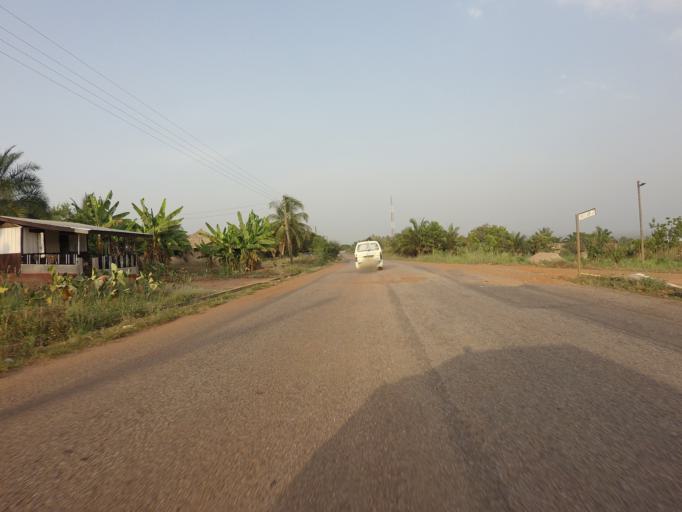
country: GH
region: Volta
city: Ho
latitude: 6.5644
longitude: 0.3001
